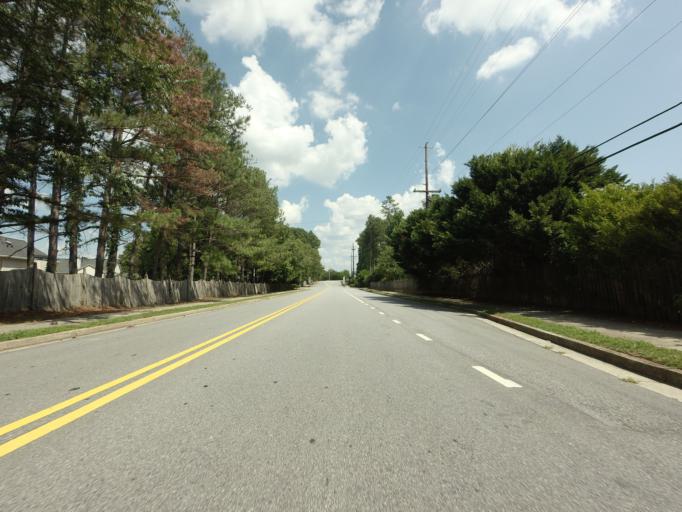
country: US
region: Georgia
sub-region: Fulton County
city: Johns Creek
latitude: 34.0490
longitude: -84.2125
